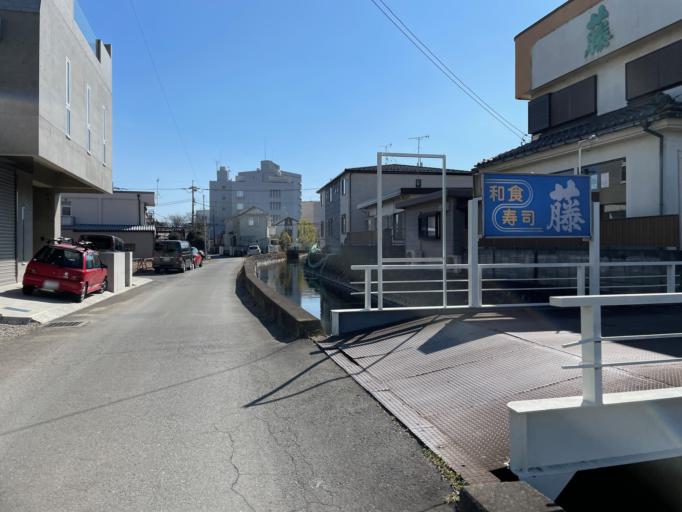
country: JP
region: Tokyo
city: Hino
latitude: 35.6886
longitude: 139.3729
